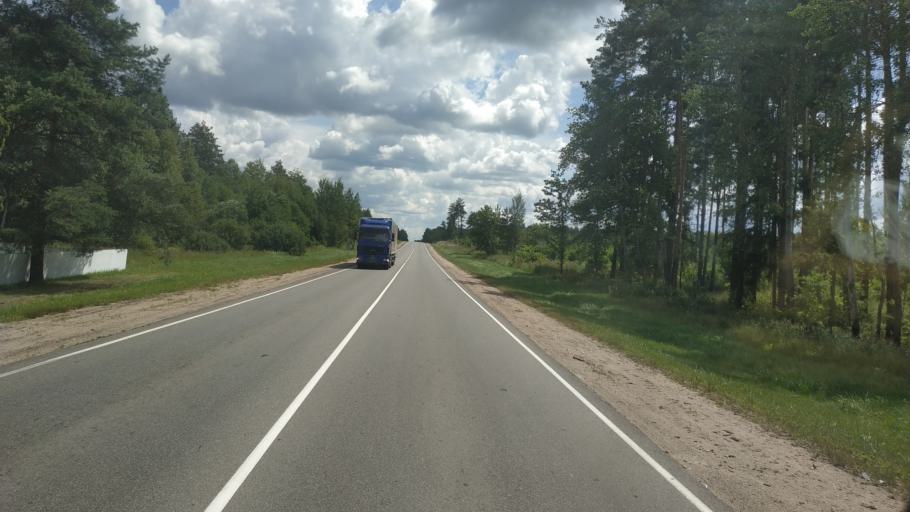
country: BY
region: Mogilev
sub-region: Mahilyowski Rayon
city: Veyno
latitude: 53.8283
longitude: 30.4141
